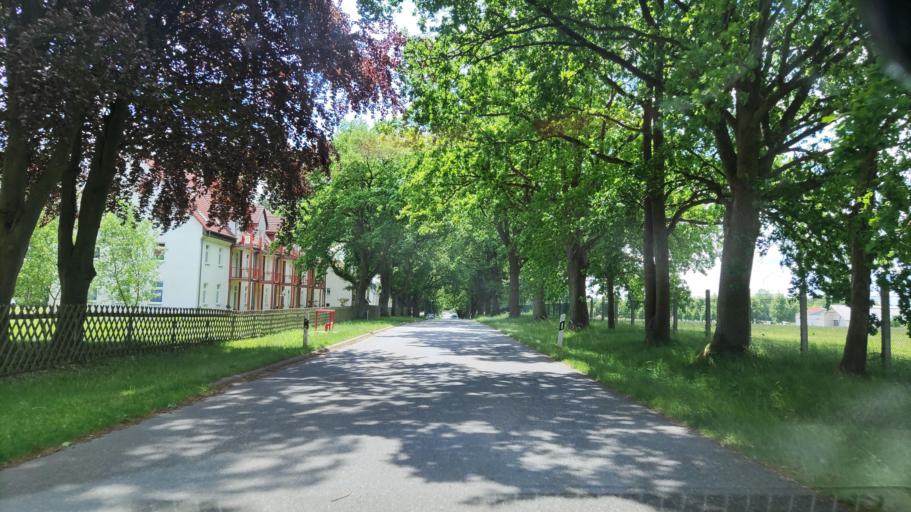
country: DE
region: Mecklenburg-Vorpommern
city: Lubtheen
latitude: 53.3883
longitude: 11.0544
